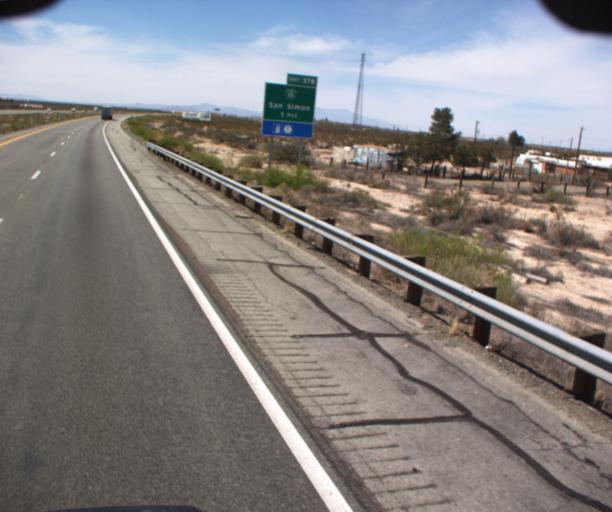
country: US
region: New Mexico
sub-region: Hidalgo County
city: Lordsburg
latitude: 32.2642
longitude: -109.2310
